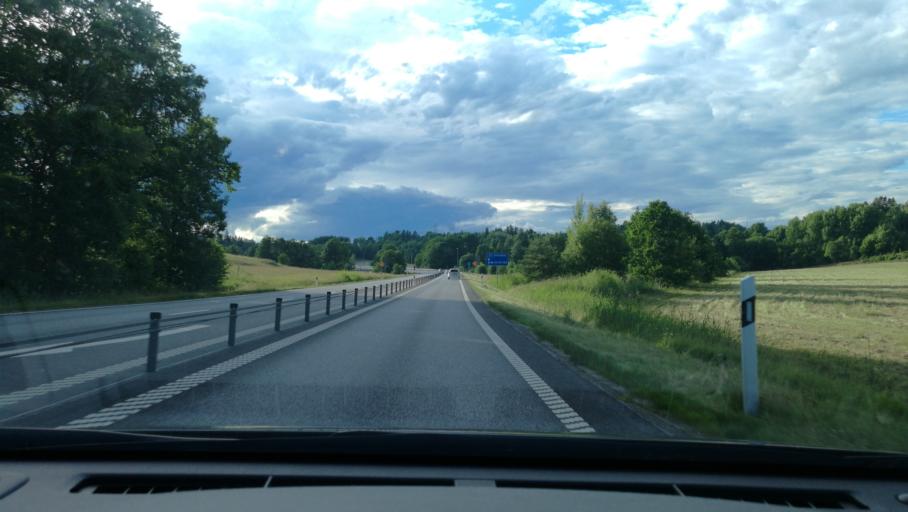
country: SE
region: OEstergoetland
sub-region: Norrkopings Kommun
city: Svartinge
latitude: 58.6882
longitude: 15.9295
